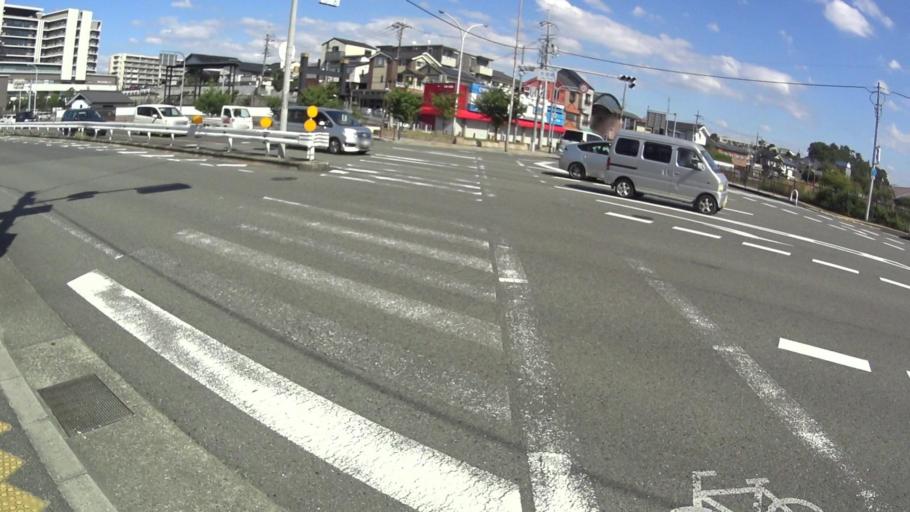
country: JP
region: Ehime
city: Kihoku-cho
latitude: 33.3844
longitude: 132.8301
